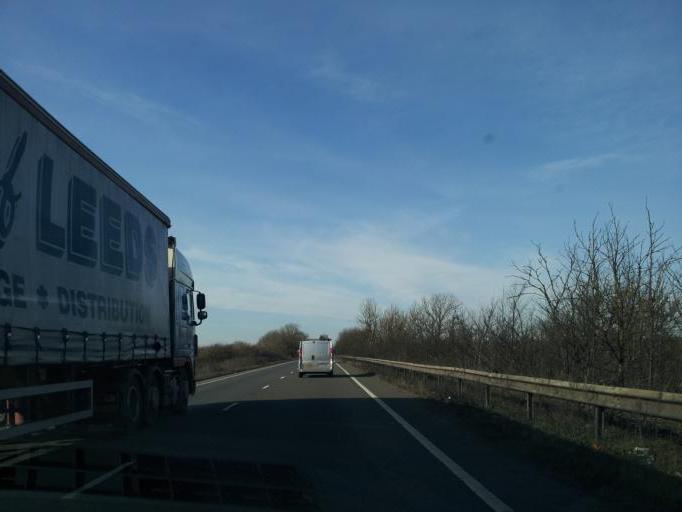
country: GB
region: England
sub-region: District of Rutland
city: Tickencote
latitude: 52.6819
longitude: -0.5458
